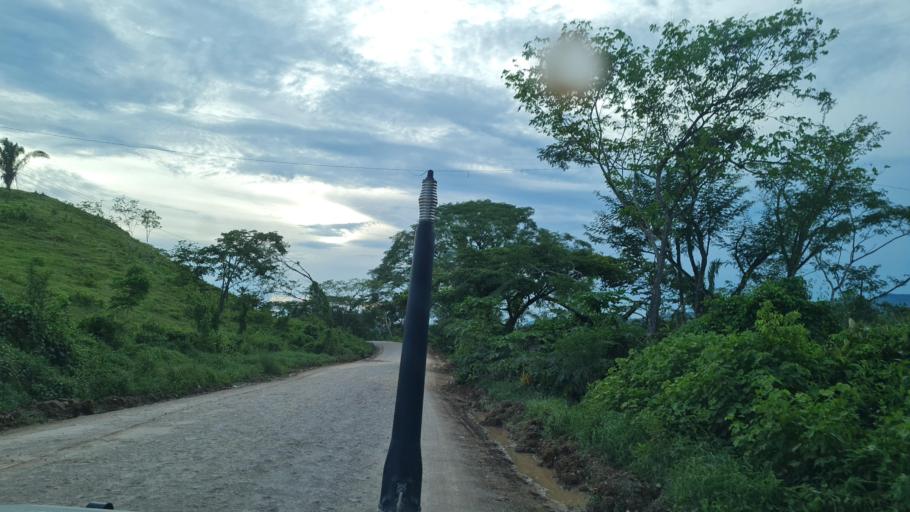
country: NI
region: Atlantico Norte (RAAN)
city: Siuna
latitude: 13.6859
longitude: -84.6080
